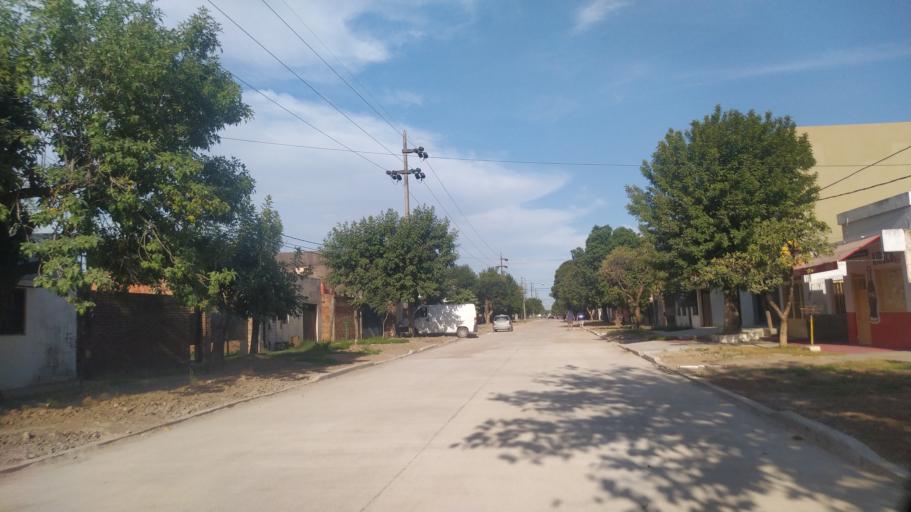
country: AR
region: Corrientes
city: Corrientes
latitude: -27.4806
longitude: -58.8099
